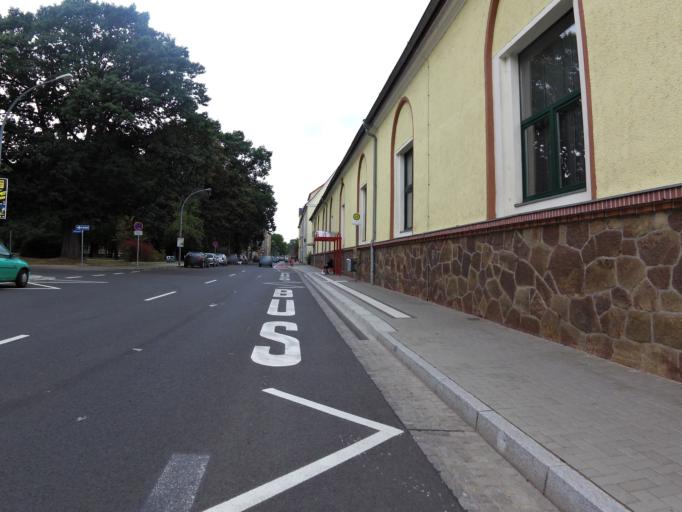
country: DE
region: Saxony
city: Dobeln
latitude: 51.1210
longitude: 13.1131
